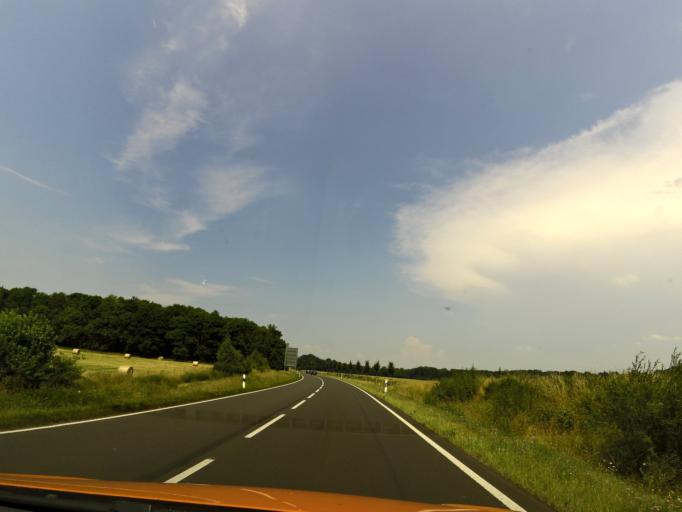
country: DE
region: Brandenburg
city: Pritzwalk
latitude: 53.1653
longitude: 12.1841
